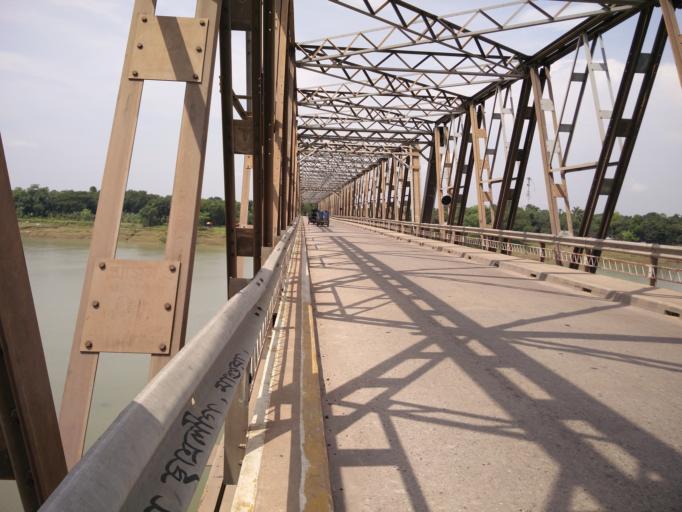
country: BD
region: Khulna
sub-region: Magura
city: Magura
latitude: 23.5413
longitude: 89.5168
